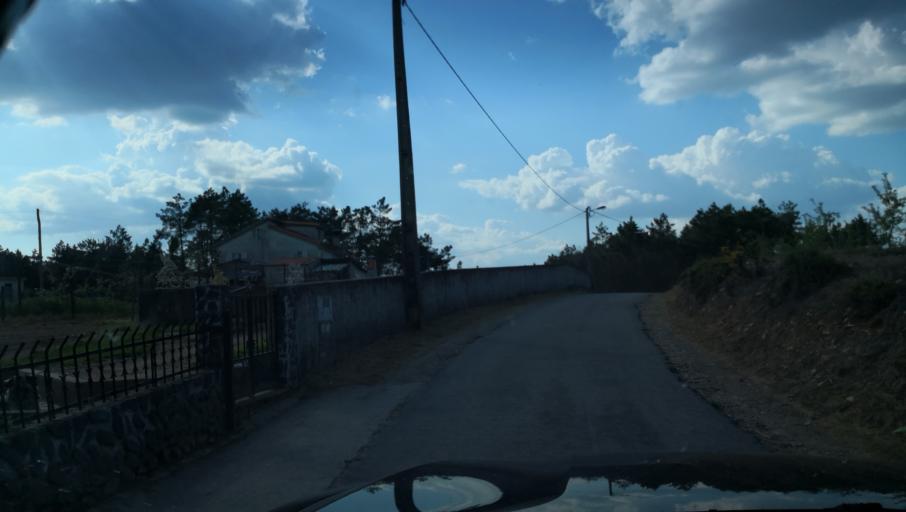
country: PT
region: Vila Real
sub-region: Sabrosa
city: Vilela
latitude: 41.2436
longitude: -7.6598
